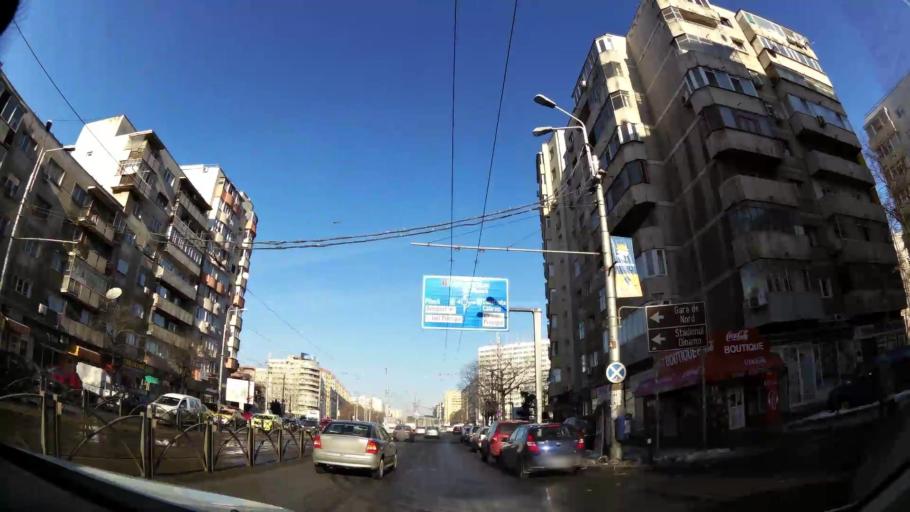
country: RO
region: Bucuresti
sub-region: Municipiul Bucuresti
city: Bucharest
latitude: 44.4483
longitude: 26.1236
